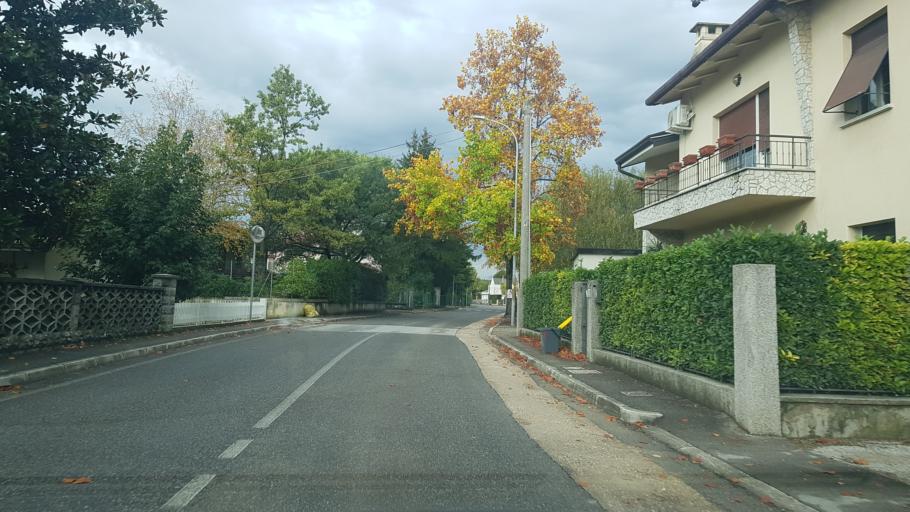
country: IT
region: Friuli Venezia Giulia
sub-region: Provincia di Gorizia
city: Ronchi dei Legionari
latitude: 45.8260
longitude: 13.5121
